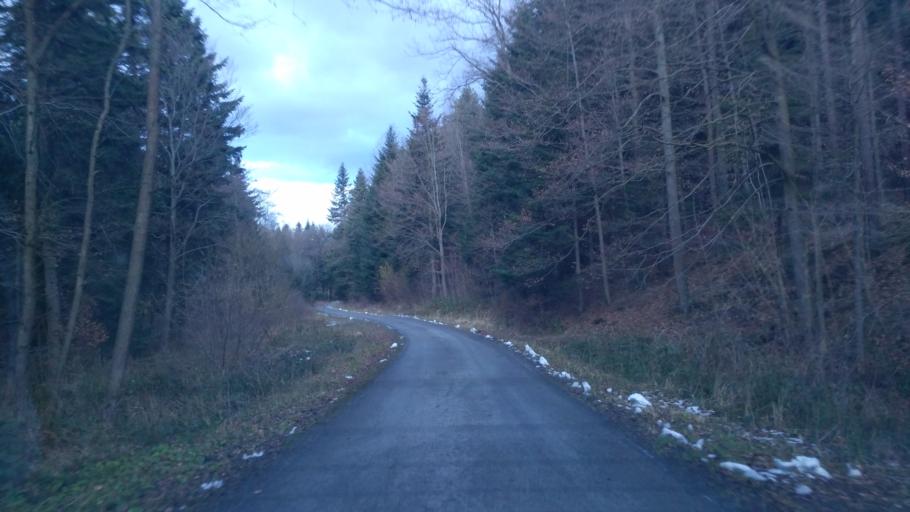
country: PL
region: Subcarpathian Voivodeship
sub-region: Powiat strzyzowski
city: Konieczkowa
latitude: 49.8252
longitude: 21.9449
